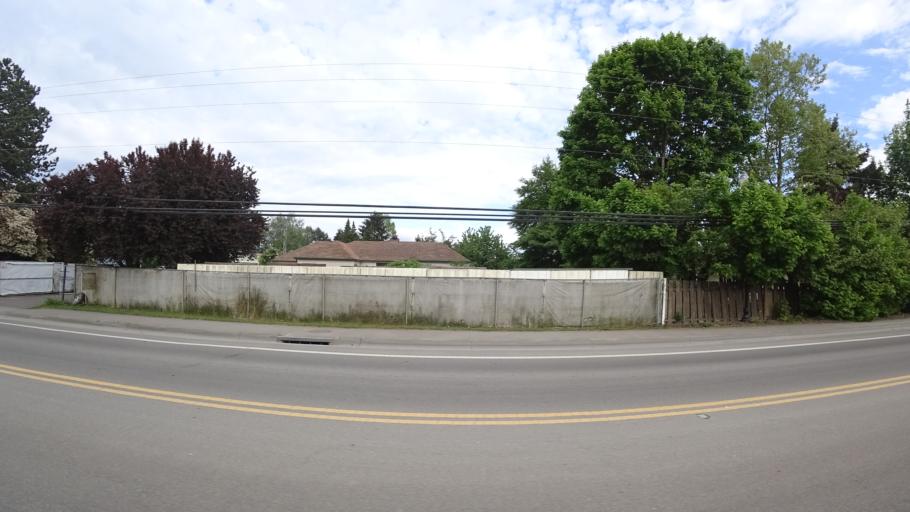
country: US
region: Oregon
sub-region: Washington County
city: Hillsboro
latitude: 45.4989
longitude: -122.9664
